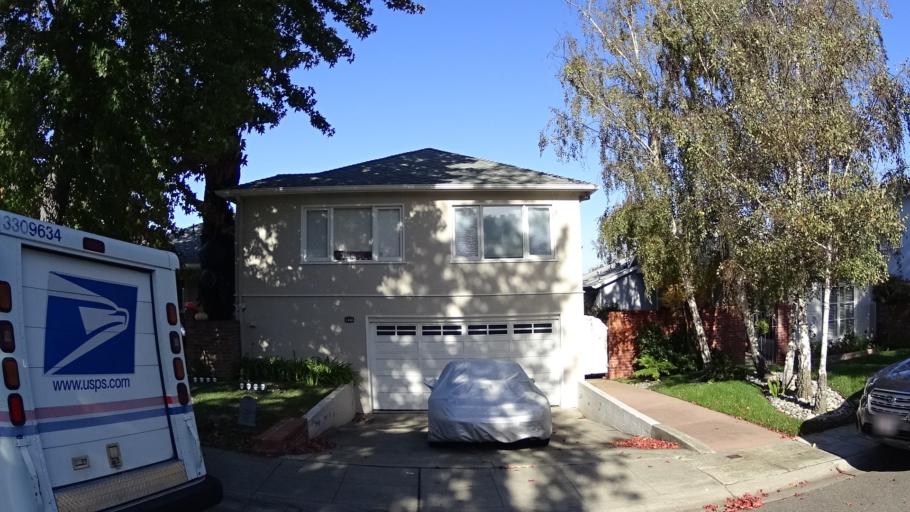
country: US
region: California
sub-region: San Mateo County
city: Millbrae
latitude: 37.5907
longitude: -122.3802
